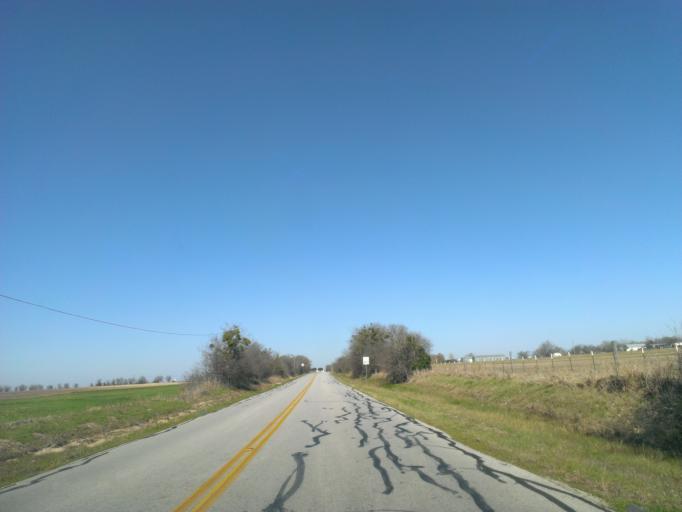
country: US
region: Texas
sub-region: Williamson County
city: Georgetown
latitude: 30.6518
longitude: -97.5782
